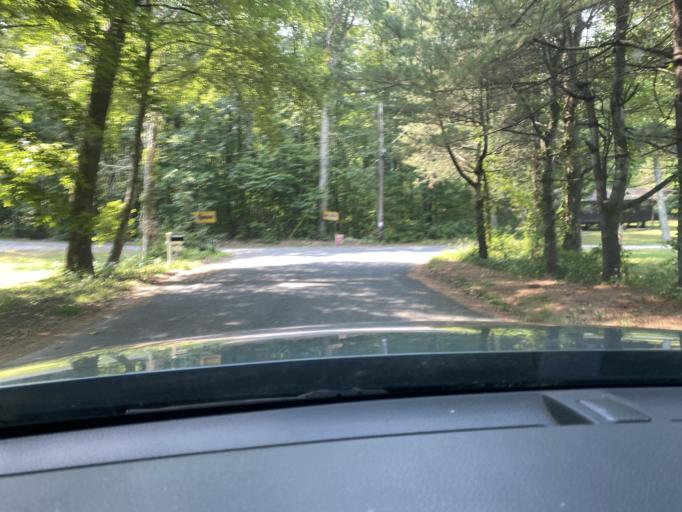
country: US
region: Connecticut
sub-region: Tolland County
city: Hebron
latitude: 41.6386
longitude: -72.2998
